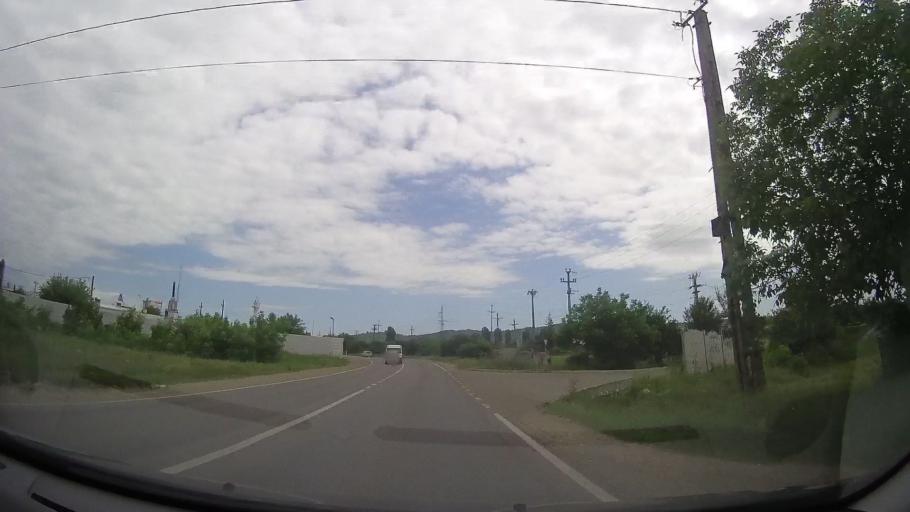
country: RO
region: Prahova
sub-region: Comuna Blejoiu
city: Blejoi
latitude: 45.0179
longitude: 26.0174
